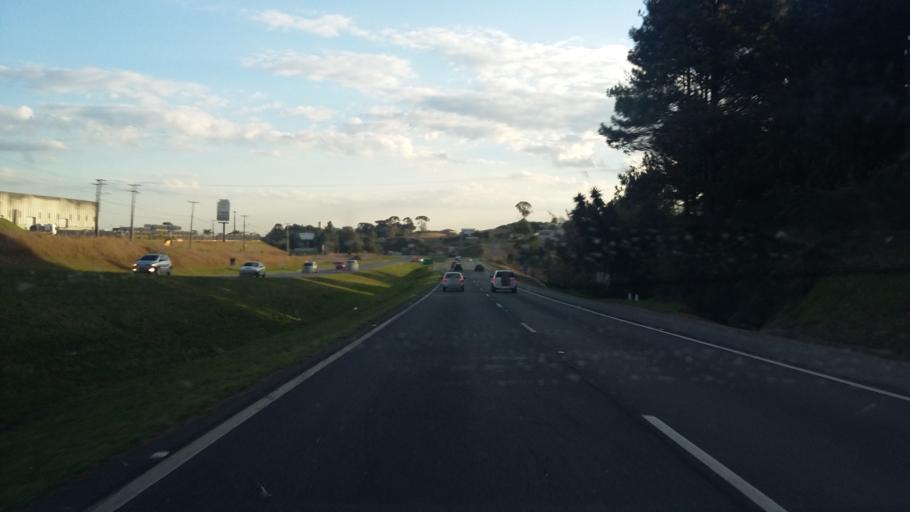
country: BR
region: Parana
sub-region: Campo Largo
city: Campo Largo
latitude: -25.4348
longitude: -49.4400
